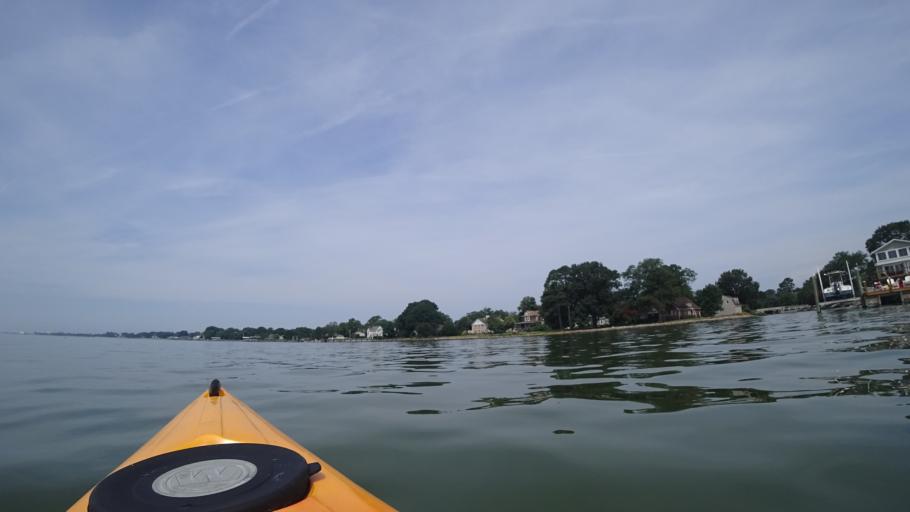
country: US
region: Virginia
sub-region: City of Hampton
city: Hampton
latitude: 36.9979
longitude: -76.3729
